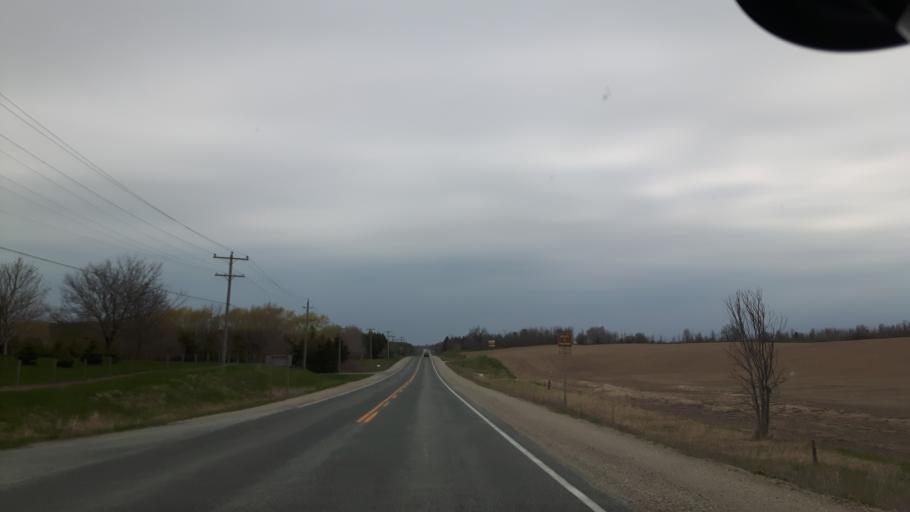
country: CA
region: Ontario
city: Goderich
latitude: 43.6615
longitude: -81.6185
